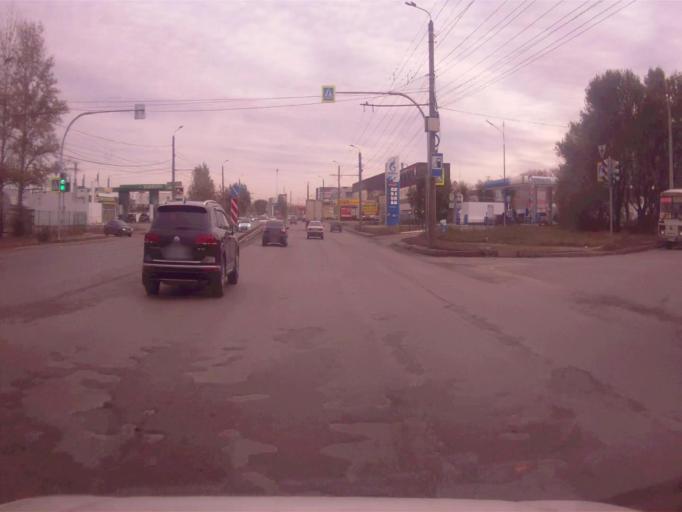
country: RU
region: Chelyabinsk
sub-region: Gorod Chelyabinsk
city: Chelyabinsk
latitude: 55.1408
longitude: 61.4544
